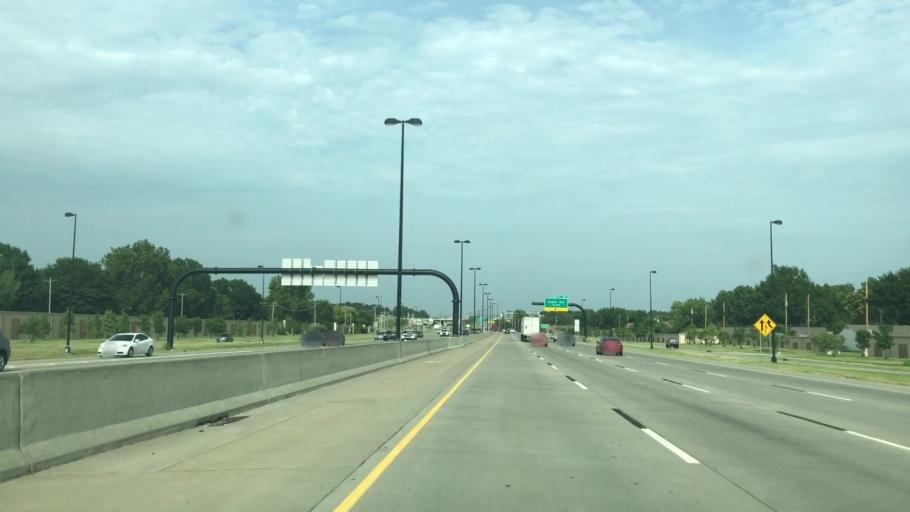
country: US
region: Oklahoma
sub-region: Tulsa County
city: Jenks
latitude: 36.0896
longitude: -95.9711
